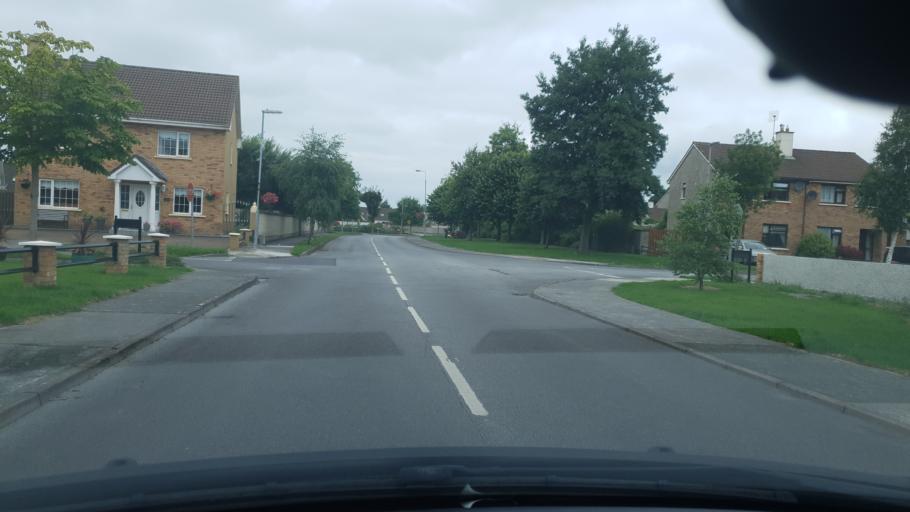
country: IE
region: Munster
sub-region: Ciarrai
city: Tralee
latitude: 52.2583
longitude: -9.6834
